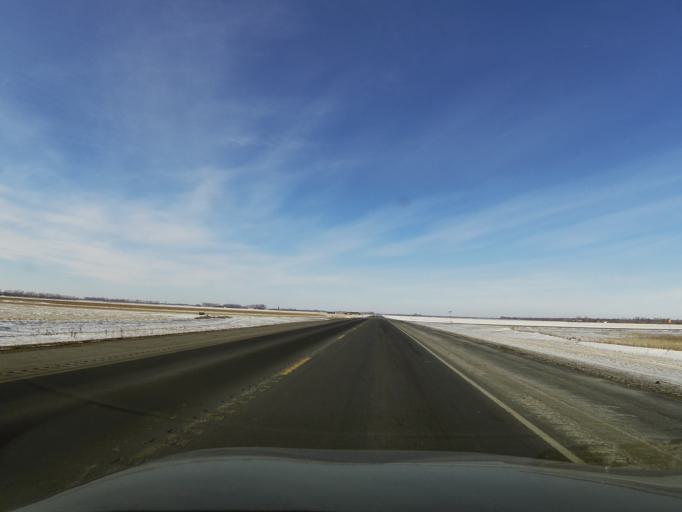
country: US
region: North Dakota
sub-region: Walsh County
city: Grafton
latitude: 48.4126
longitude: -97.4684
